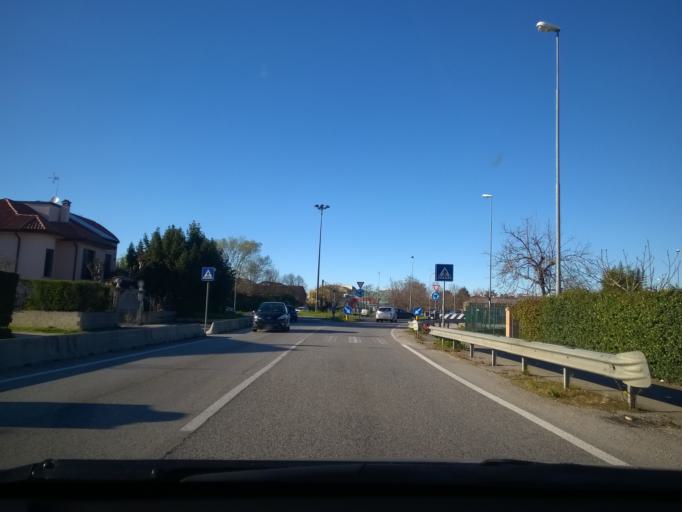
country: IT
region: Veneto
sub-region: Provincia di Venezia
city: Mirano
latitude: 45.4818
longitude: 12.1075
